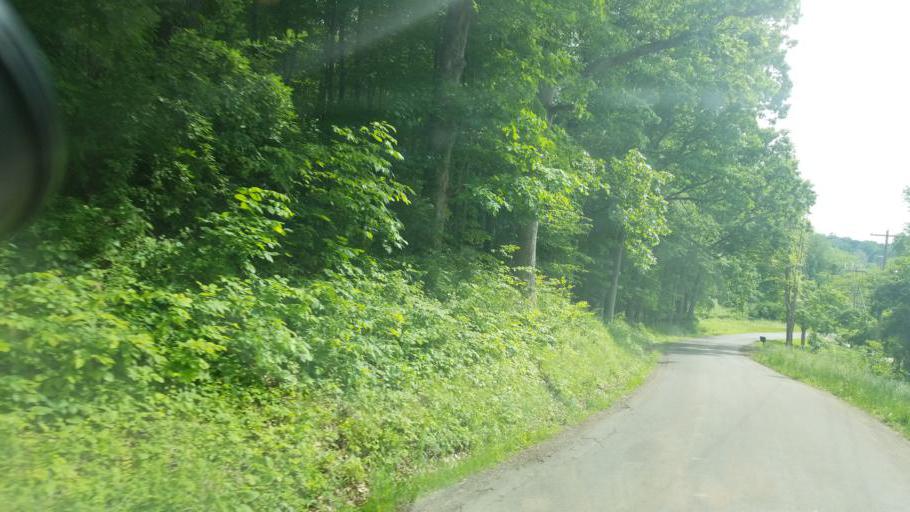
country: US
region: Ohio
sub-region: Knox County
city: Gambier
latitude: 40.3908
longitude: -82.4124
